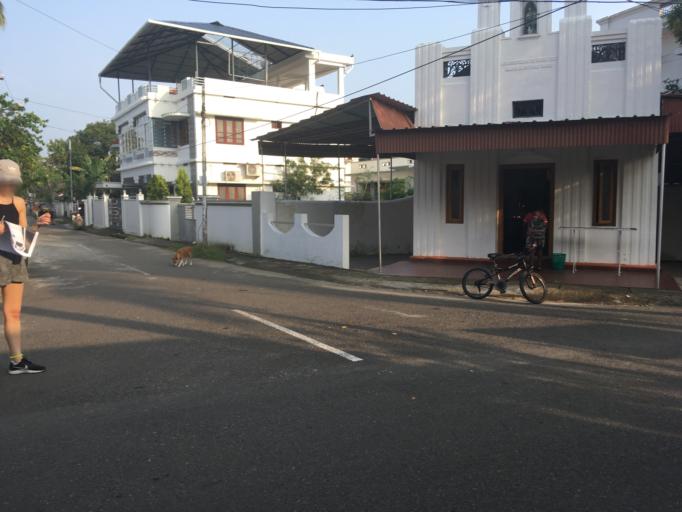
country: IN
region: Kerala
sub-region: Ernakulam
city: Cochin
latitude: 9.9594
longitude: 76.2406
